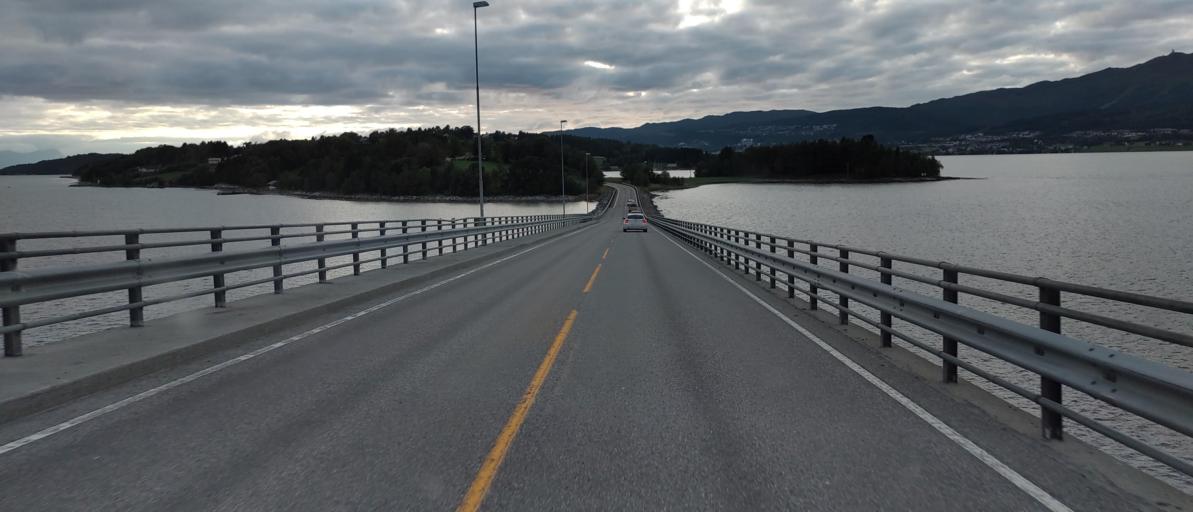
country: NO
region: More og Romsdal
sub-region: Molde
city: Hjelset
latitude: 62.7309
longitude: 7.3524
